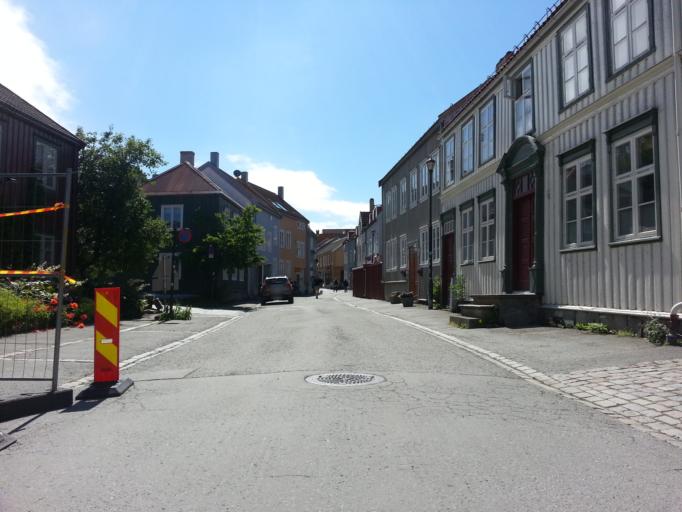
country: NO
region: Sor-Trondelag
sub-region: Trondheim
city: Trondheim
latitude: 63.4301
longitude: 10.4046
